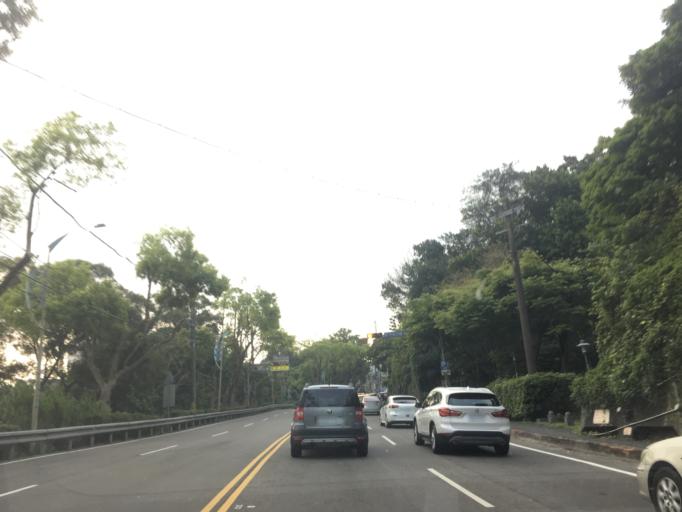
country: TW
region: Taiwan
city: Daxi
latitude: 24.8860
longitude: 121.2883
